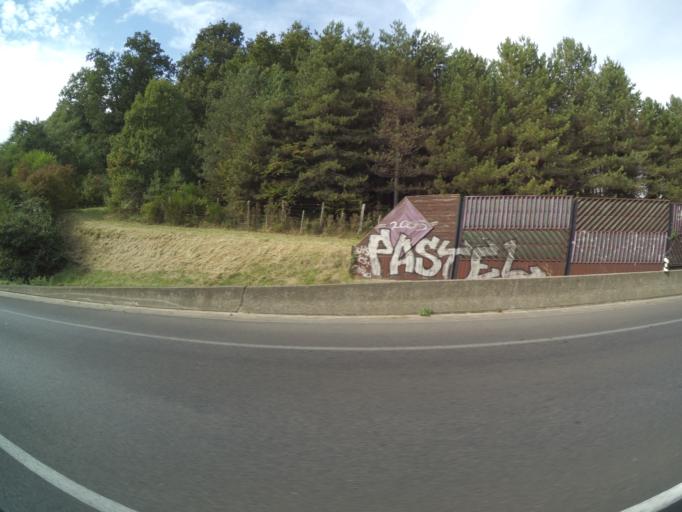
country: FR
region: Pays de la Loire
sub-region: Departement de Maine-et-Loire
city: Saumur
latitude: 47.2570
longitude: -0.0982
